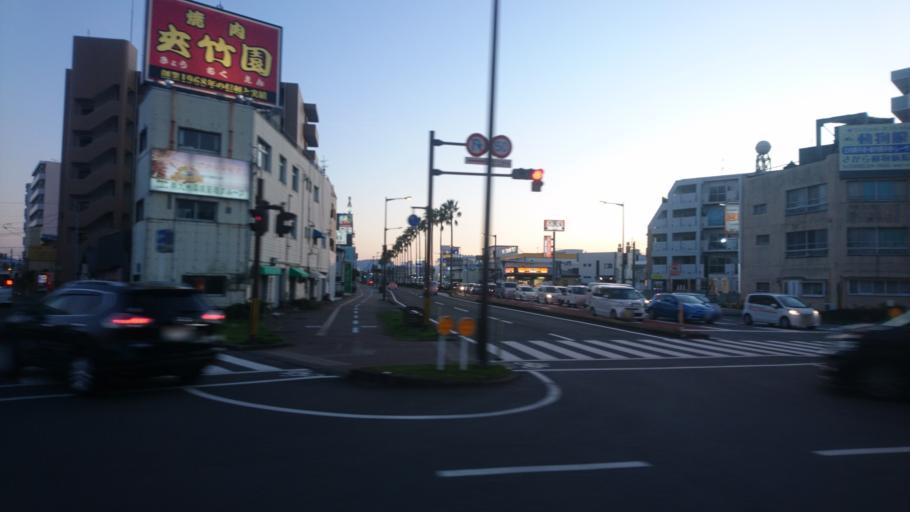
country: JP
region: Miyazaki
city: Miyazaki-shi
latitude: 31.8980
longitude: 131.4182
